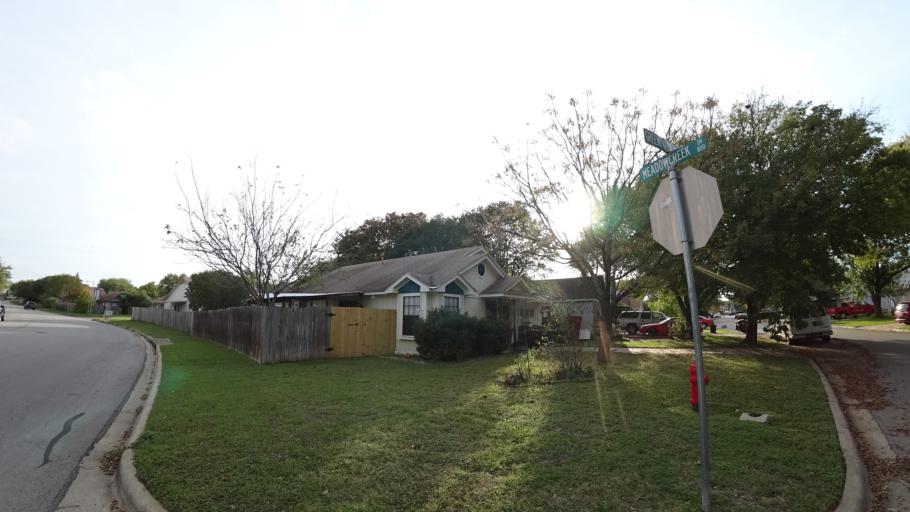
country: US
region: Texas
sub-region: Williamson County
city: Round Rock
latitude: 30.5019
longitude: -97.6651
